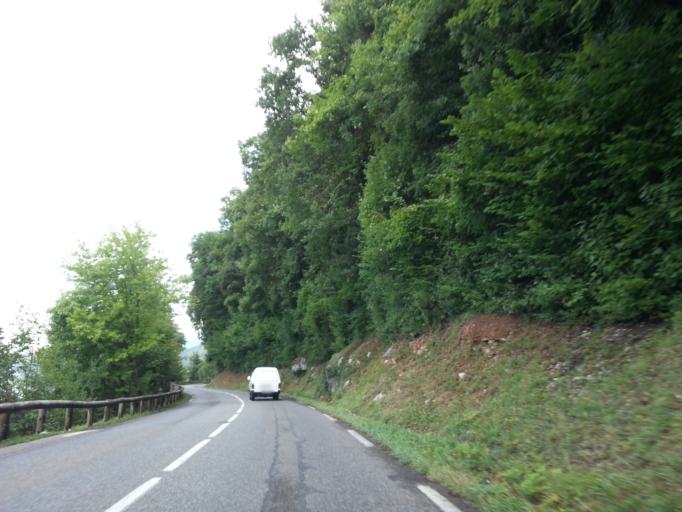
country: FR
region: Rhone-Alpes
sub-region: Departement de la Haute-Savoie
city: Talloires
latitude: 45.8112
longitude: 6.2312
